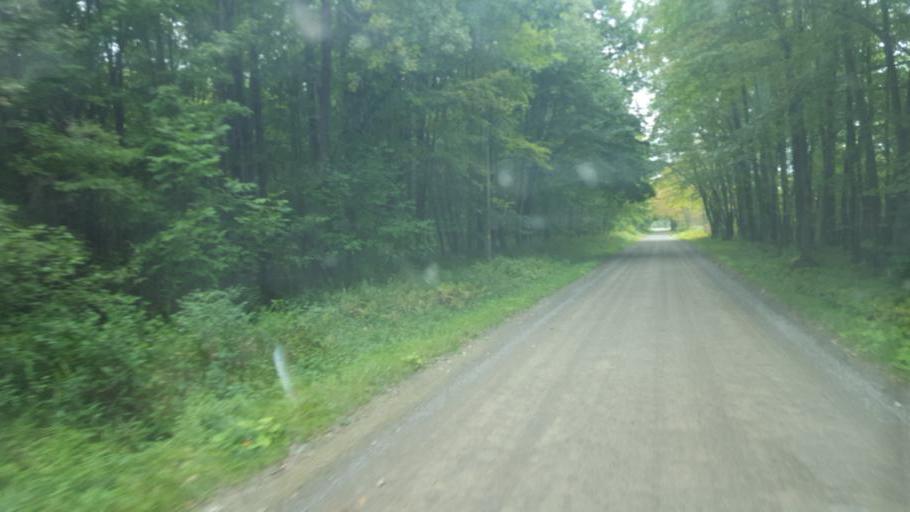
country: US
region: Pennsylvania
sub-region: Crawford County
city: Pymatuning Central
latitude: 41.5435
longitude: -80.4323
